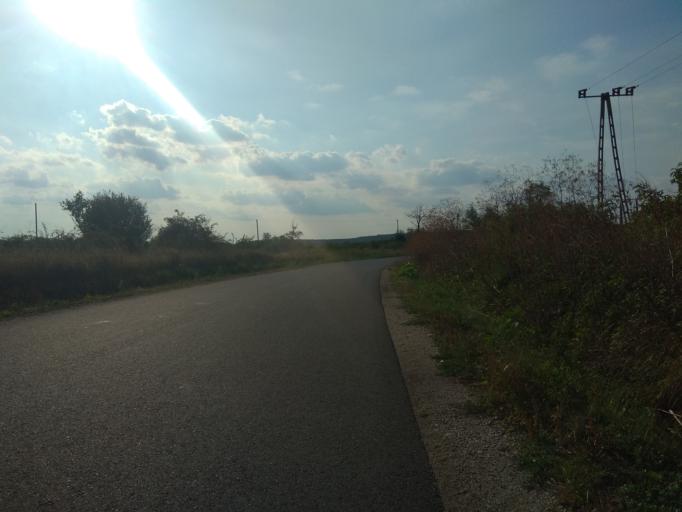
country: HU
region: Borsod-Abauj-Zemplen
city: Harsany
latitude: 47.8978
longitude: 20.7470
